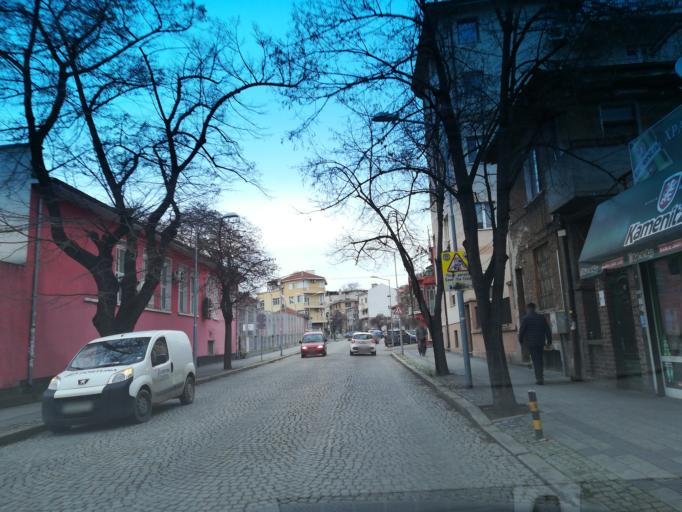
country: BG
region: Plovdiv
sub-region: Obshtina Plovdiv
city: Plovdiv
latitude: 42.1458
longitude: 24.7436
